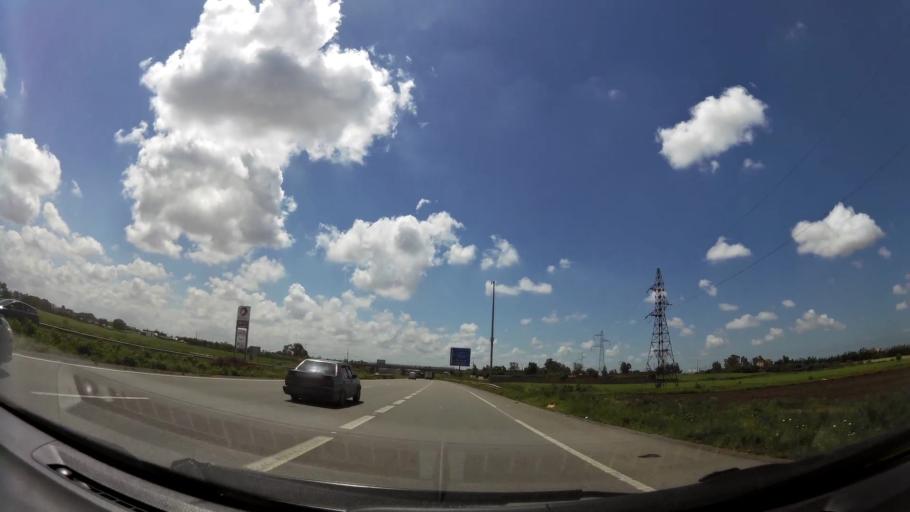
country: MA
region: Grand Casablanca
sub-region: Nouaceur
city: Bouskoura
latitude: 33.5085
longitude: -7.6134
